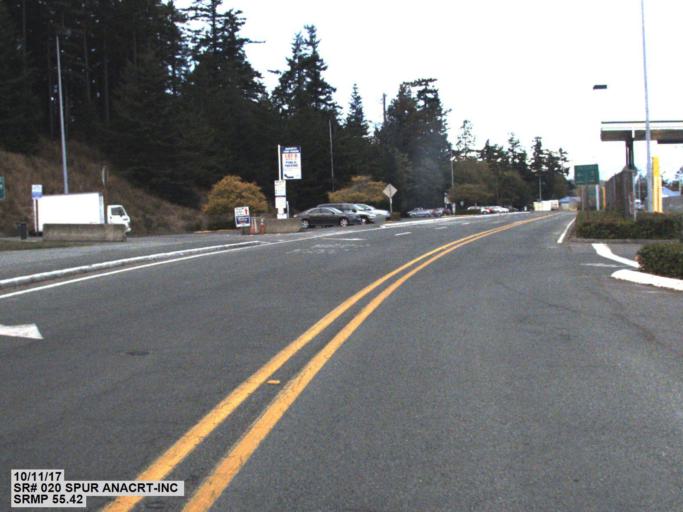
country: US
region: Washington
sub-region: Jefferson County
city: Port Hadlock-Irondale
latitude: 48.0677
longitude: -122.8196
